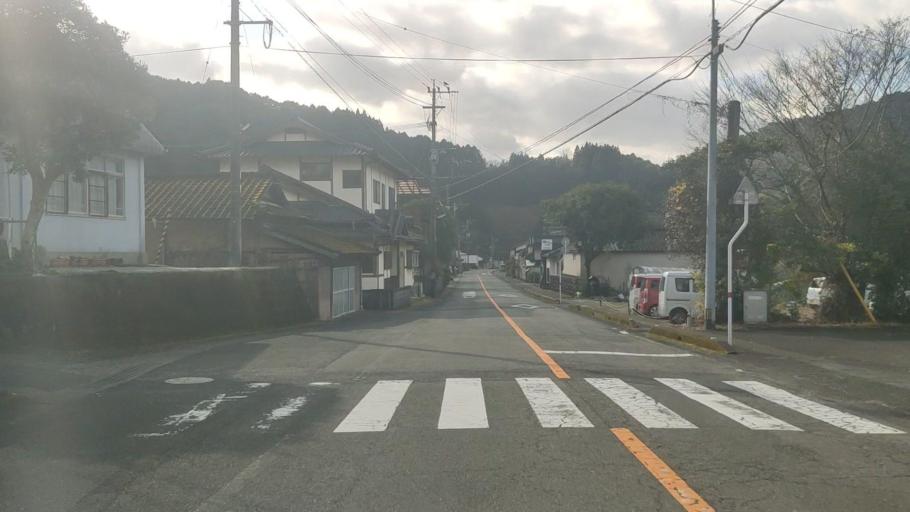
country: JP
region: Kumamoto
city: Hitoyoshi
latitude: 32.3068
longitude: 130.8478
